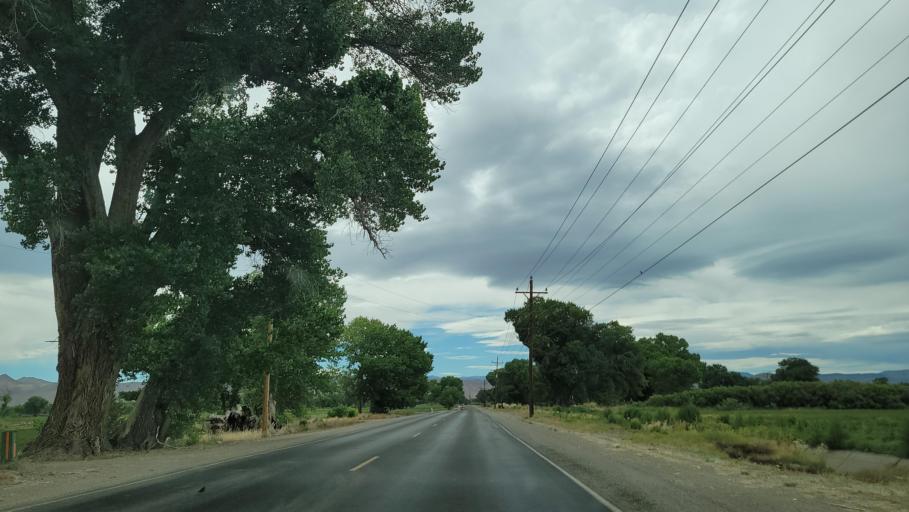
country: US
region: Nevada
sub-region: Lyon County
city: Yerington
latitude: 39.0482
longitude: -119.1531
